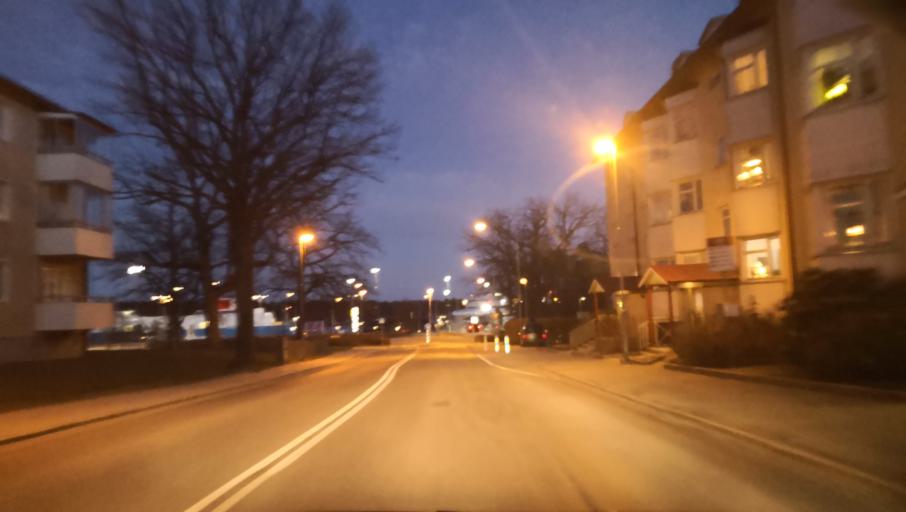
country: SE
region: Stockholm
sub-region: Nynashamns Kommun
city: Nynashamn
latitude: 58.9103
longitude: 17.9533
